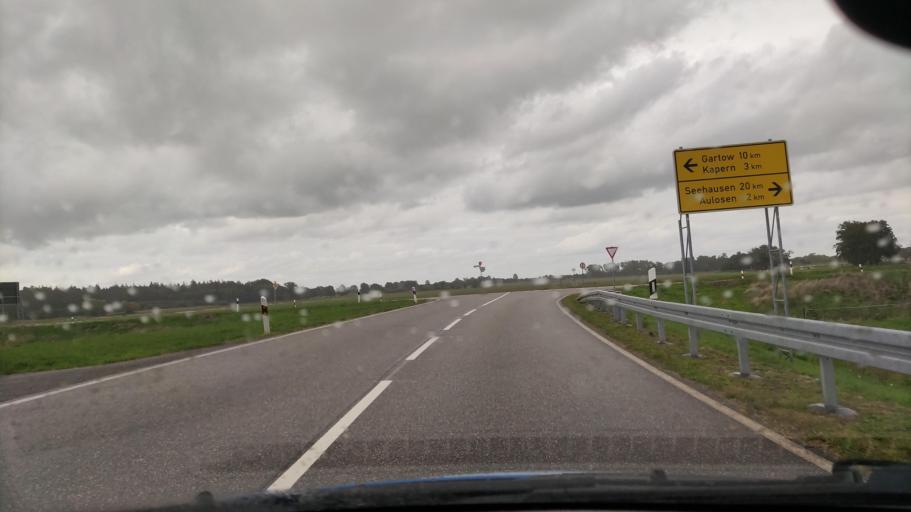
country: DE
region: Brandenburg
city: Lanz
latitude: 52.9937
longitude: 11.5487
